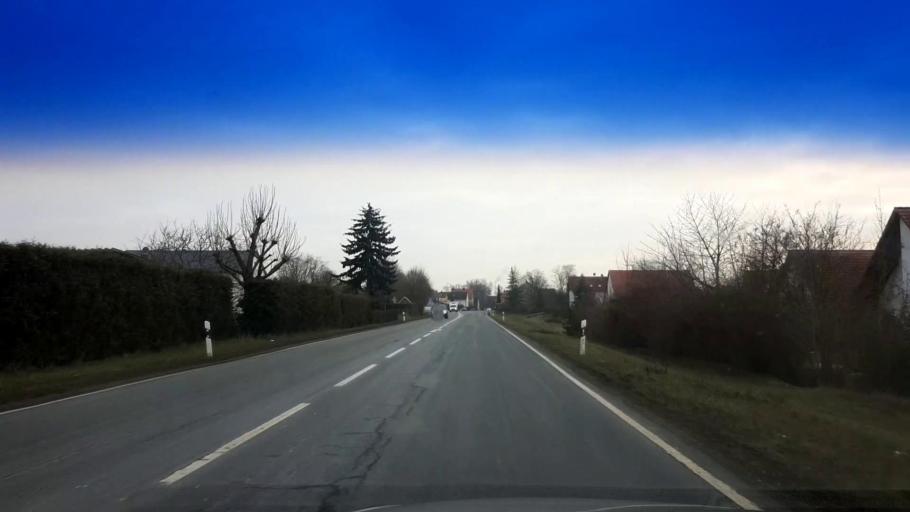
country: DE
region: Bavaria
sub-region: Upper Franconia
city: Altendorf
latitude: 49.8016
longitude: 11.0085
